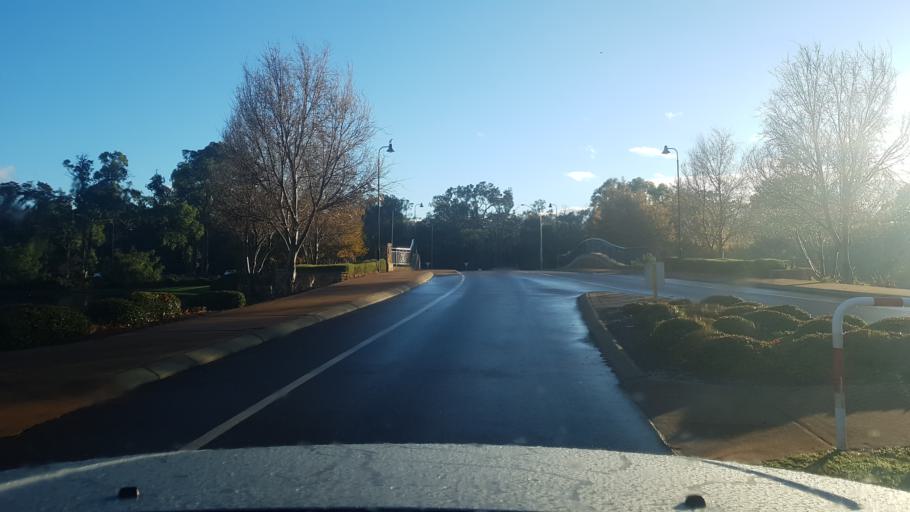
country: AU
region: Western Australia
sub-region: Busselton
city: Vasse
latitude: -33.6771
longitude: 115.2591
